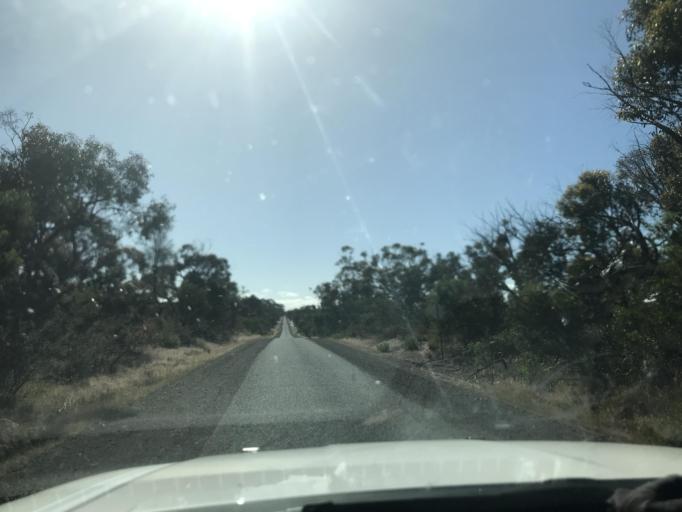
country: AU
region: Victoria
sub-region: Horsham
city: Horsham
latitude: -37.0223
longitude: 141.6757
